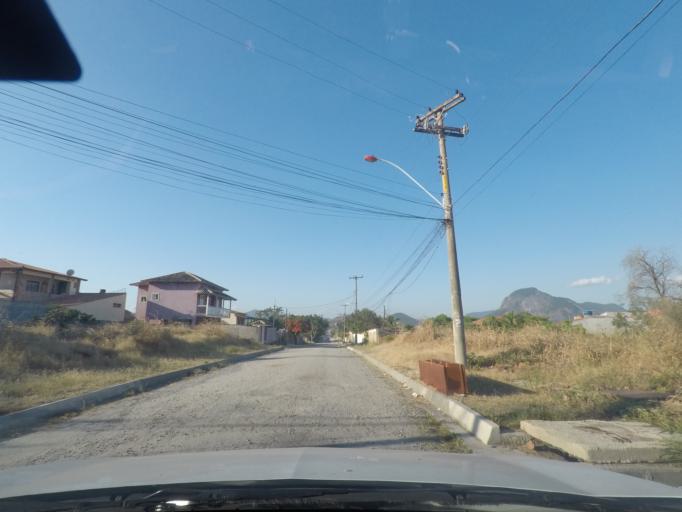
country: BR
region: Rio de Janeiro
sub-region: Marica
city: Marica
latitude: -22.9670
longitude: -42.9370
